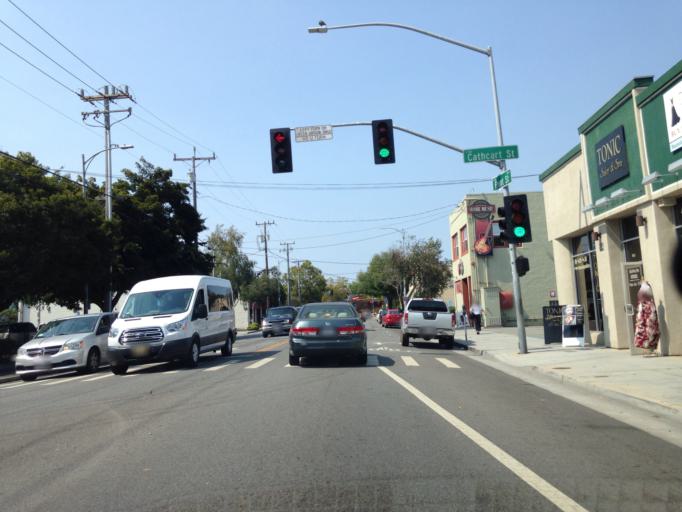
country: US
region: California
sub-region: Santa Cruz County
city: Santa Cruz
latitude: 36.9719
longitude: -122.0242
